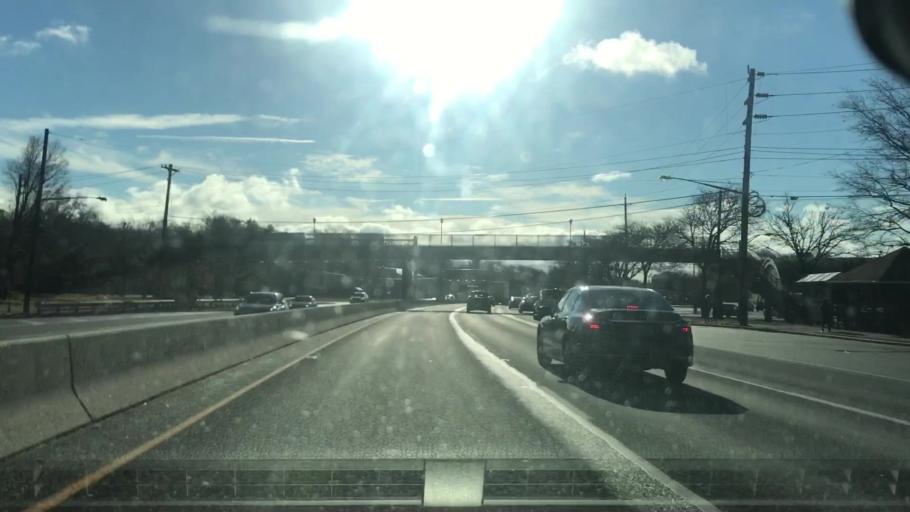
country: US
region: New Jersey
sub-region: Bergen County
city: Ho-Ho-Kus
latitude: 40.9797
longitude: -74.0841
